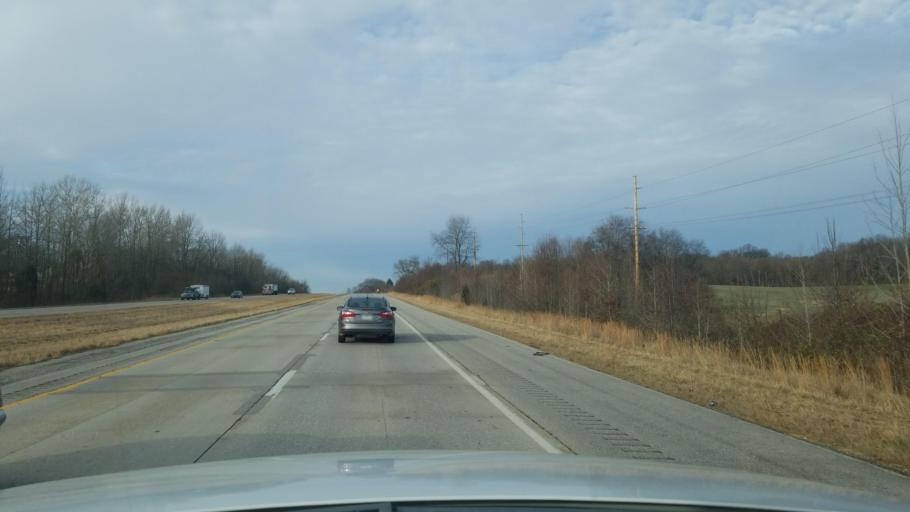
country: US
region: Indiana
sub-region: Posey County
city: Mount Vernon
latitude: 37.9426
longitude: -87.7245
